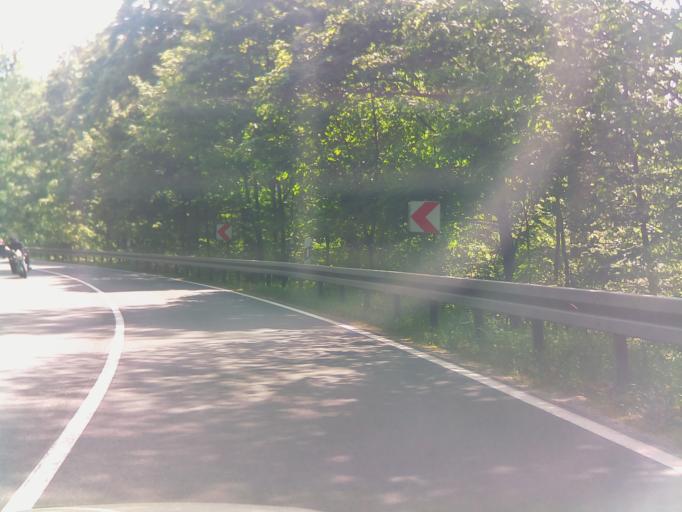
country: DE
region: Saxony-Anhalt
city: Huttenrode
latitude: 51.7254
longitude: 10.8914
